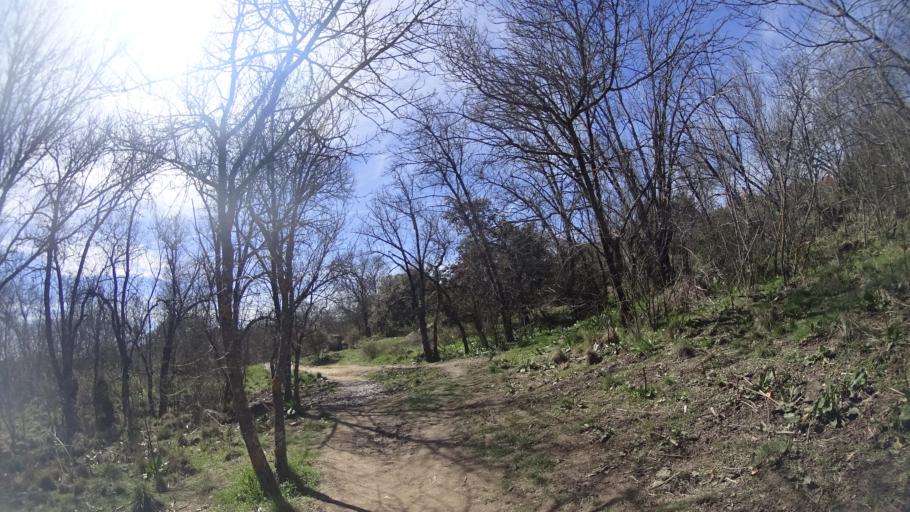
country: ES
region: Madrid
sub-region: Provincia de Madrid
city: Galapagar
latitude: 40.5933
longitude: -3.9774
